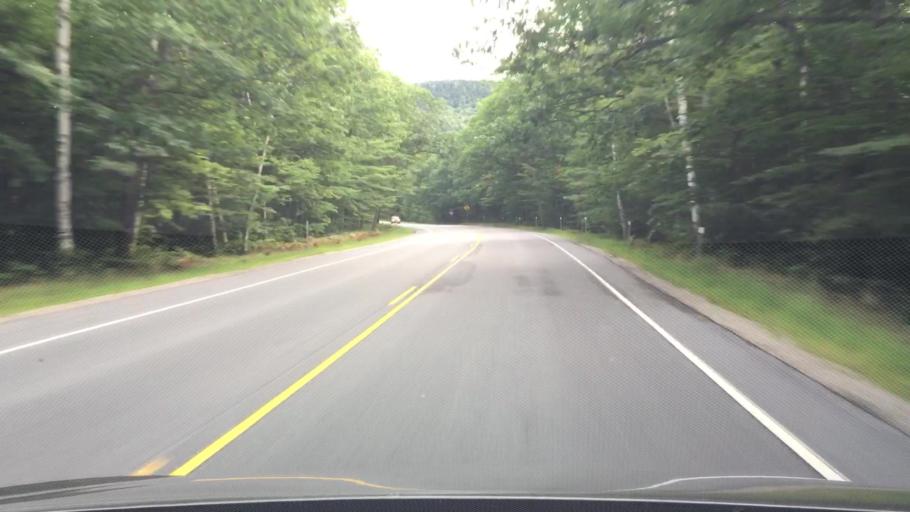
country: US
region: New Hampshire
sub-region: Carroll County
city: North Conway
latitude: 44.0096
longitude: -71.2438
